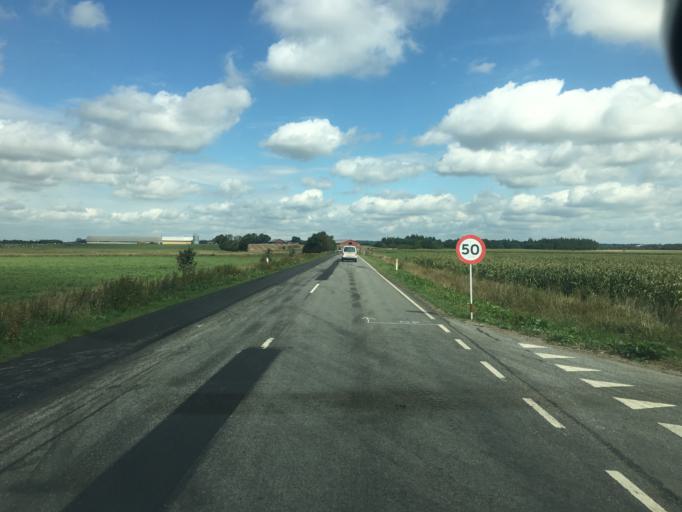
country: DK
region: South Denmark
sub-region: Tonder Kommune
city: Toftlund
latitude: 55.1081
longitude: 9.0324
